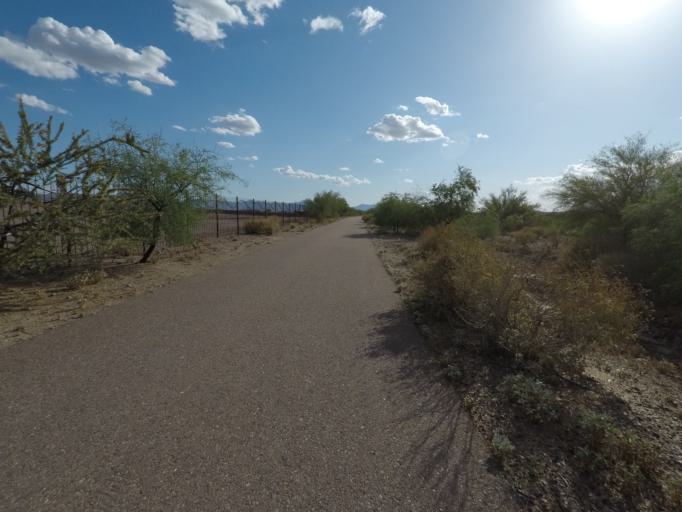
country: US
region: Arizona
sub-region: Maricopa County
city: Phoenix
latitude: 33.4200
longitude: -112.0773
